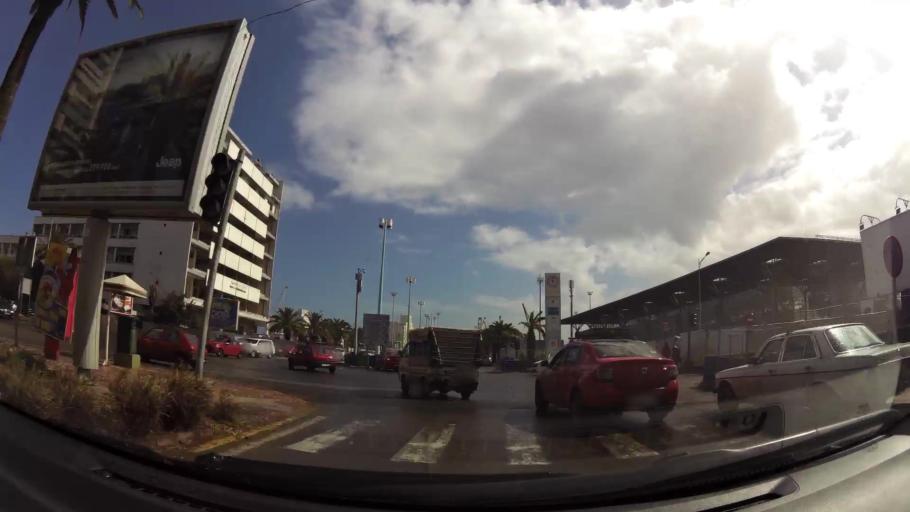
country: MA
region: Grand Casablanca
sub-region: Casablanca
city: Casablanca
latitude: 33.5992
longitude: -7.6139
